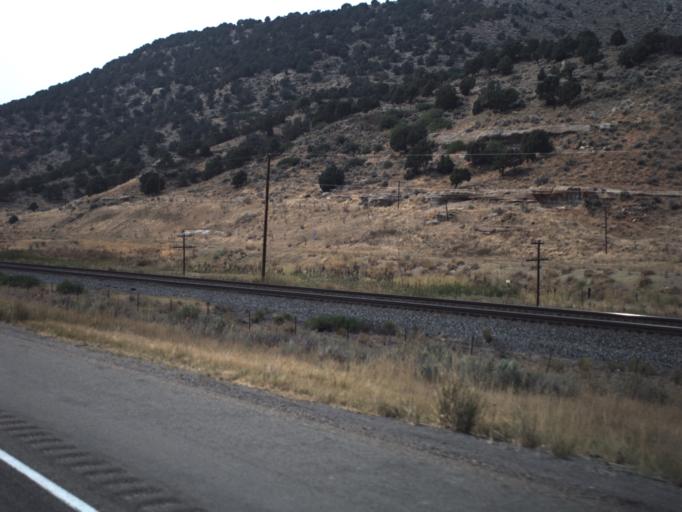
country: US
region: Utah
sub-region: Summit County
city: Coalville
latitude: 41.0446
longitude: -111.3135
